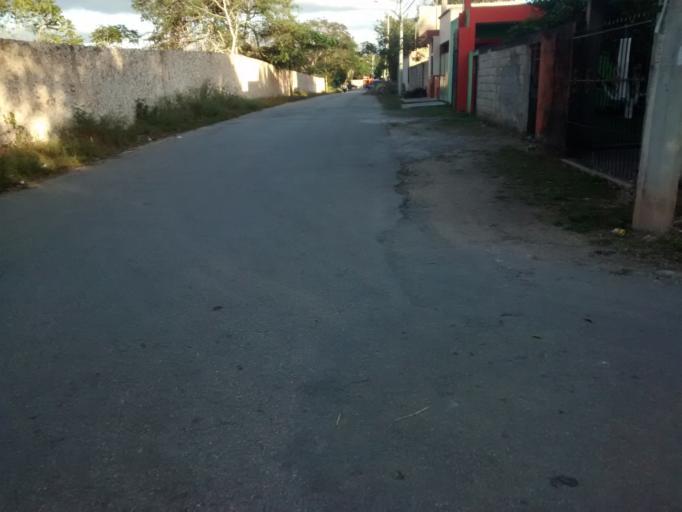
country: MX
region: Yucatan
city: Valladolid
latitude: 20.6824
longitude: -88.1847
